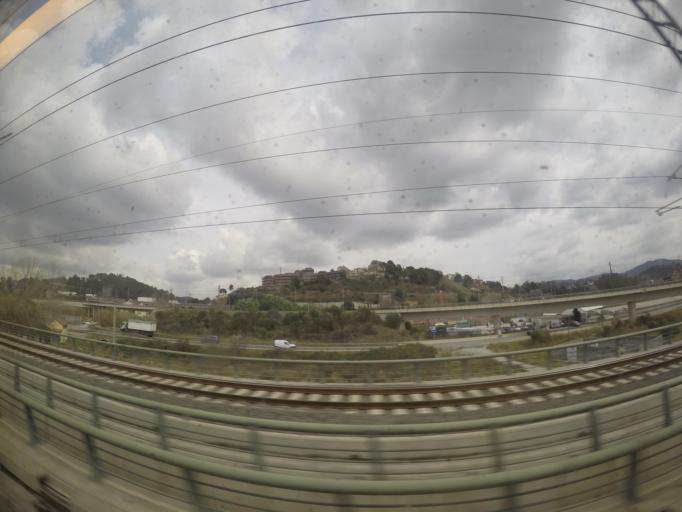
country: ES
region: Catalonia
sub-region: Provincia de Barcelona
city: Palleja
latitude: 41.4343
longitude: 2.0011
